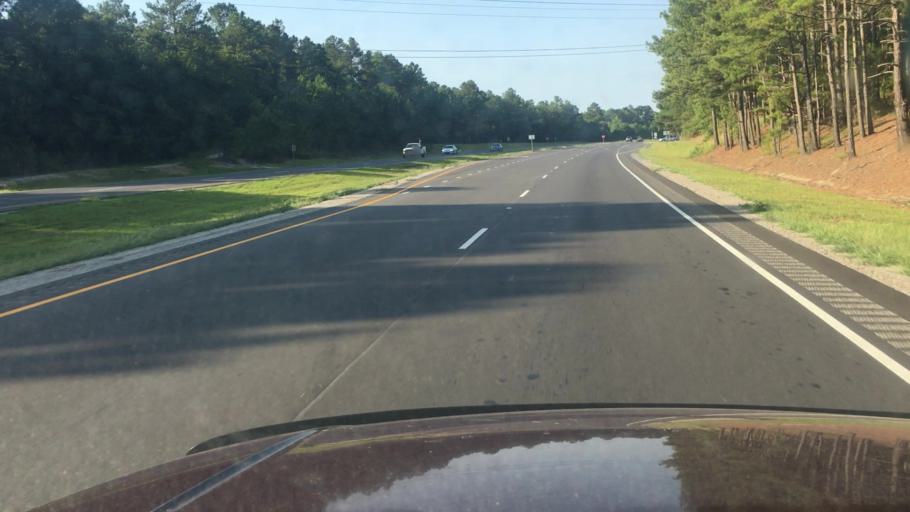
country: US
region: North Carolina
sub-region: Robeson County
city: Saint Pauls
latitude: 34.8567
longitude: -78.8499
